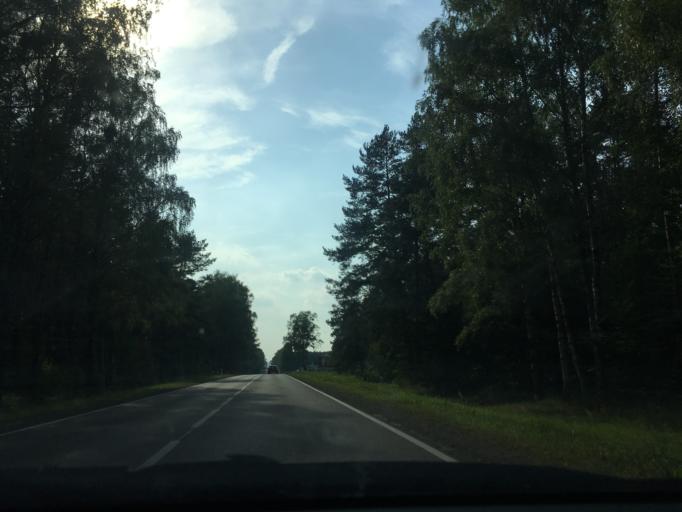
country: PL
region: Podlasie
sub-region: Powiat bialostocki
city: Suprasl
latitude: 53.1255
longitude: 23.3125
